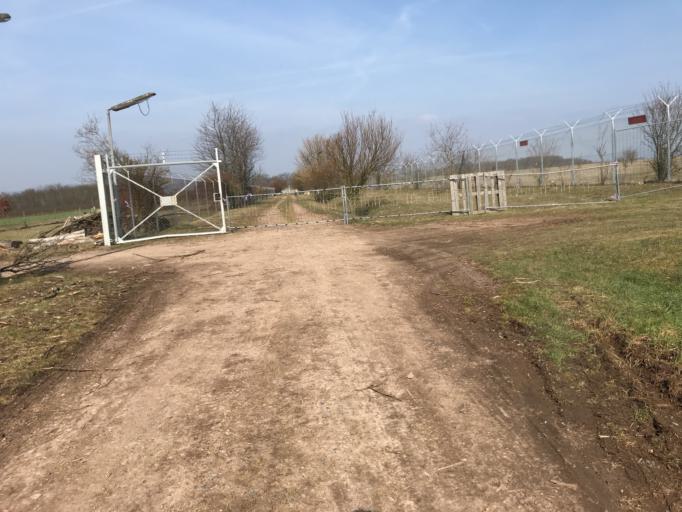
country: DE
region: Rheinland-Pfalz
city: Wackernheim
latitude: 49.9654
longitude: 8.1409
